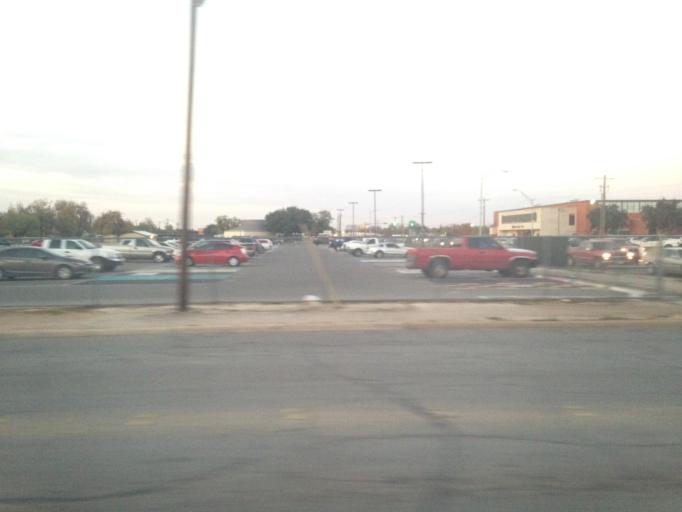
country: US
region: Texas
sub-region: Taylor County
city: Abilene
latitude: 32.4553
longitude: -99.7582
